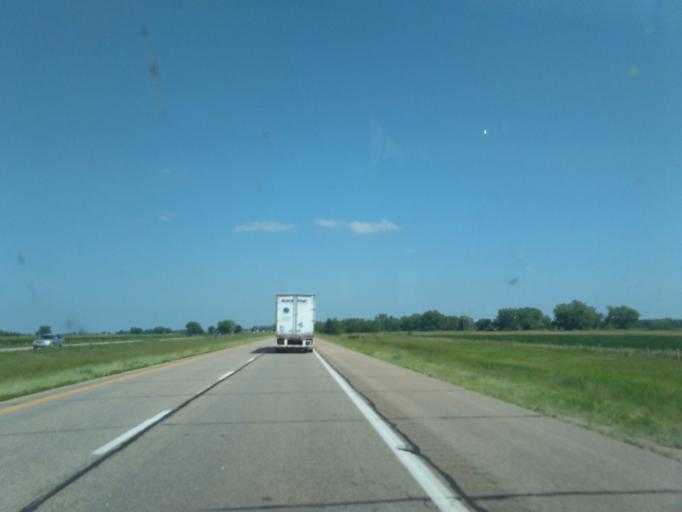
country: US
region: Nebraska
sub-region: Buffalo County
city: Kearney
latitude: 40.6872
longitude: -99.3268
